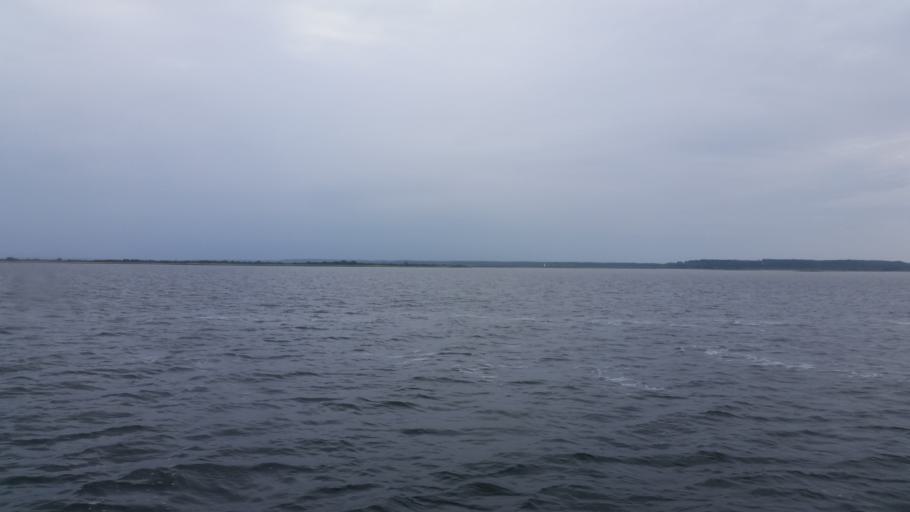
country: DE
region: Mecklenburg-Vorpommern
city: Hiddensee
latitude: 54.5731
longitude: 13.1308
